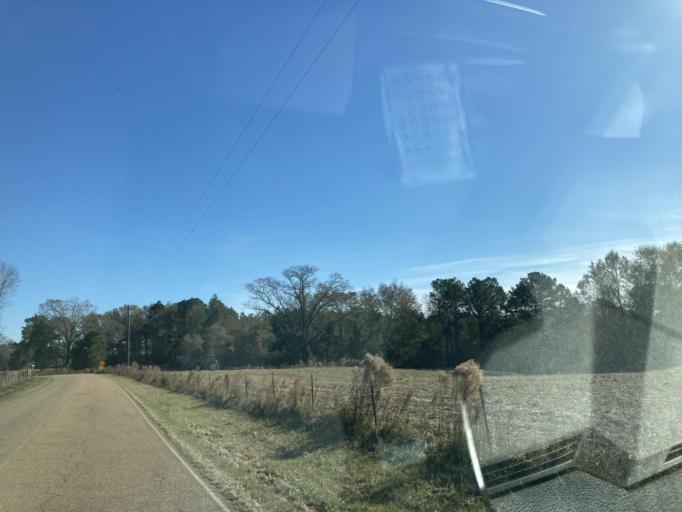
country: US
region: Mississippi
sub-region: Lamar County
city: Sumrall
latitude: 31.2664
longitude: -89.5328
